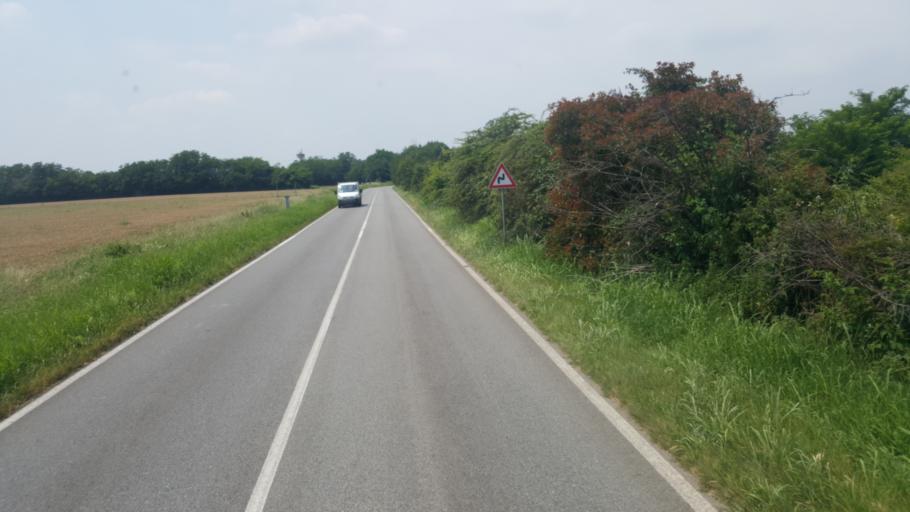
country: IT
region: Lombardy
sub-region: Provincia di Monza e Brianza
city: Cavenago di Brianza
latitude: 45.5948
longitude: 9.3998
